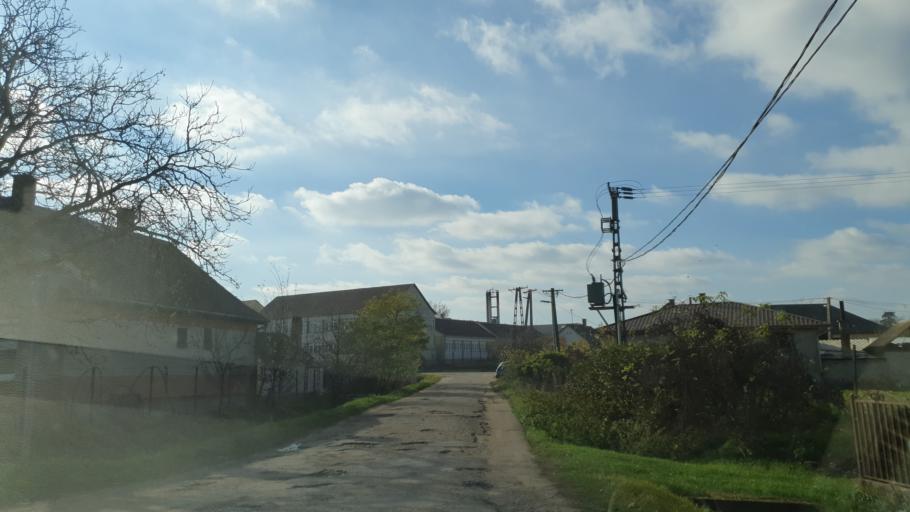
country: HU
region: Szabolcs-Szatmar-Bereg
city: Petnehaza
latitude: 48.0620
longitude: 22.0805
